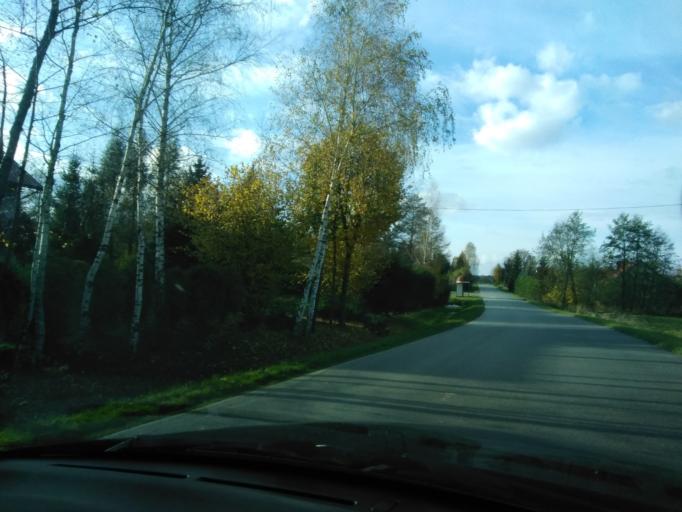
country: PL
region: Subcarpathian Voivodeship
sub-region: Powiat ropczycko-sedziszowski
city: Wielopole Skrzynskie
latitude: 49.9473
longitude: 21.6005
